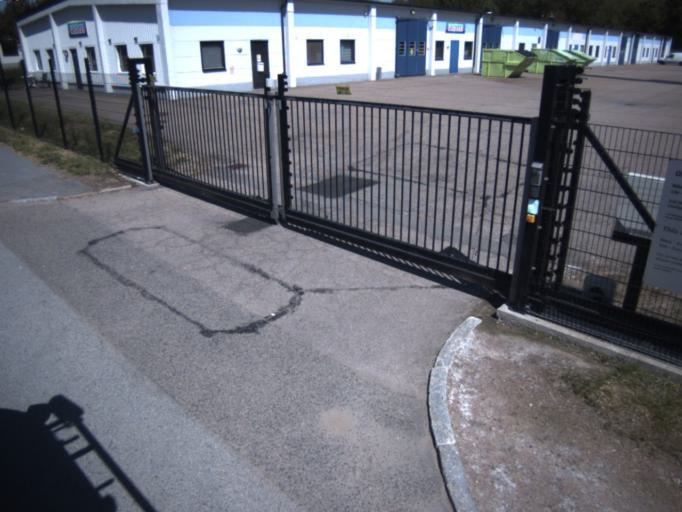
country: SE
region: Skane
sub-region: Helsingborg
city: Gantofta
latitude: 56.0073
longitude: 12.7765
